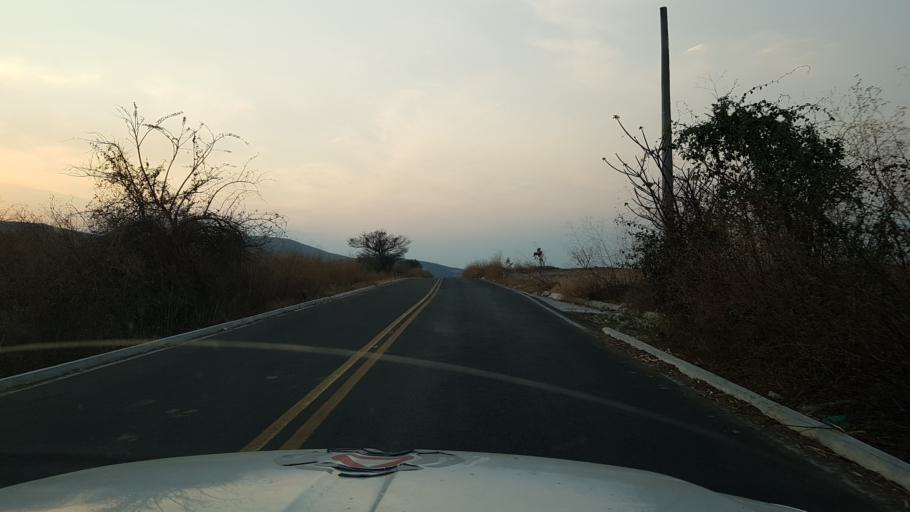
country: MX
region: Morelos
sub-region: Ayala
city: Olintepec
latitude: 18.7331
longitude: -99.0060
